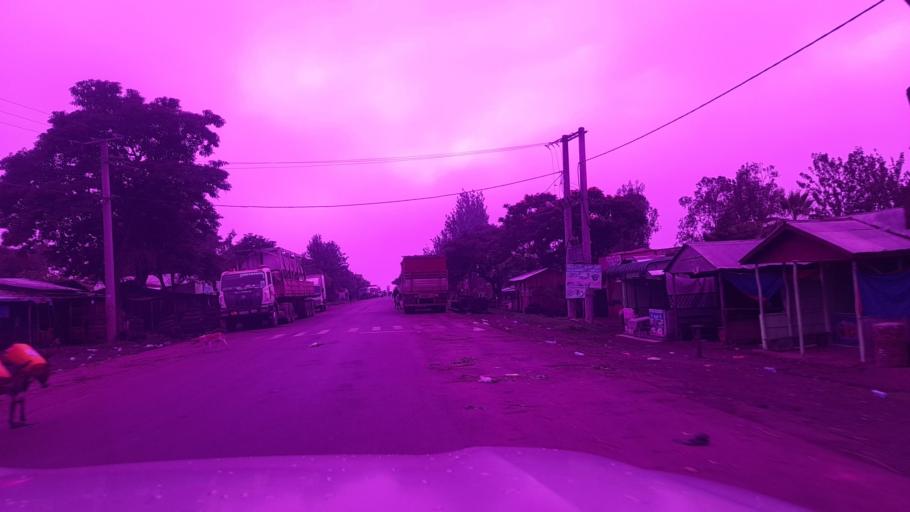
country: ET
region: Oromiya
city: Waliso
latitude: 8.1746
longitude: 37.5723
